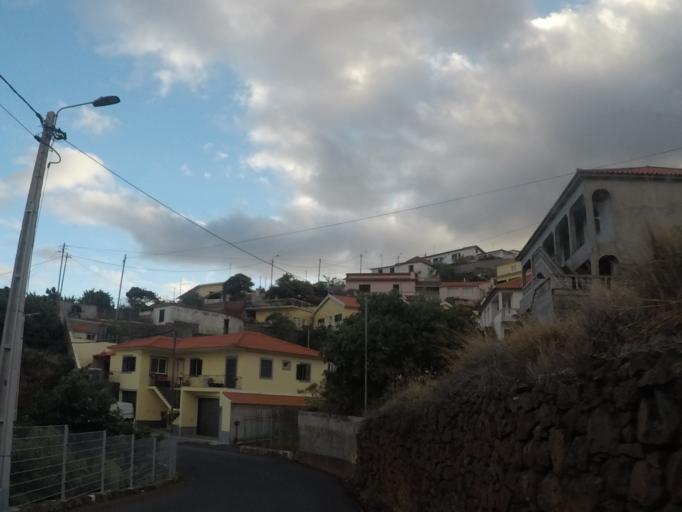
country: PT
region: Madeira
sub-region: Santa Cruz
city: Santa Cruz
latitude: 32.6731
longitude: -16.8053
